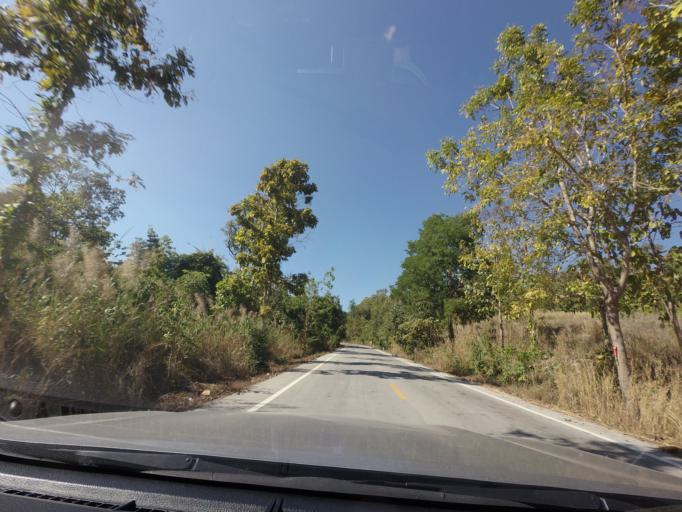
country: TH
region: Lampang
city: Chae Hom
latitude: 18.5613
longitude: 99.6250
